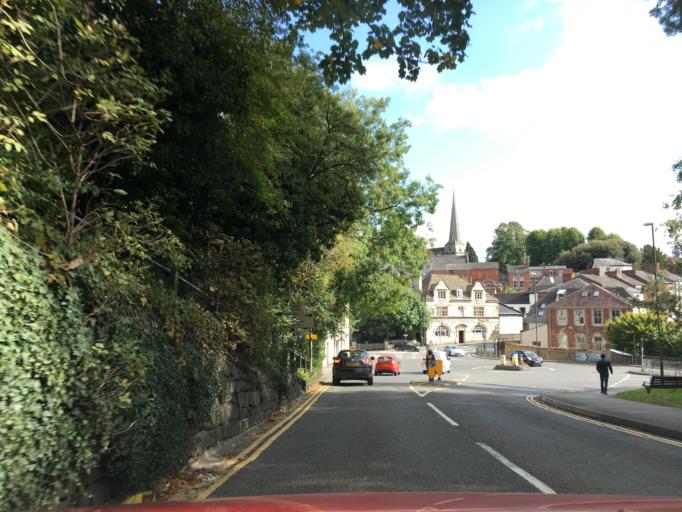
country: GB
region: England
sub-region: Gloucestershire
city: Stroud
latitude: 51.7476
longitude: -2.2181
